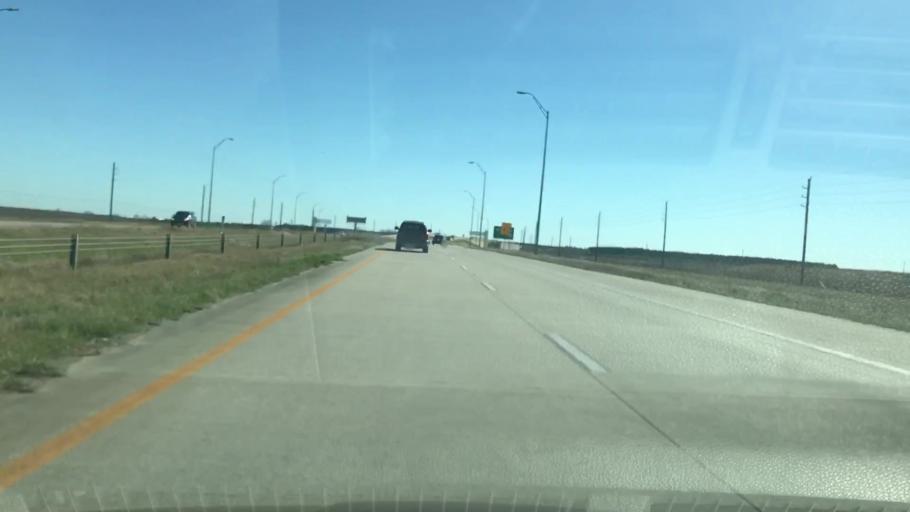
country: US
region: Texas
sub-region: Harris County
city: Cypress
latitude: 29.9108
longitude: -95.7614
